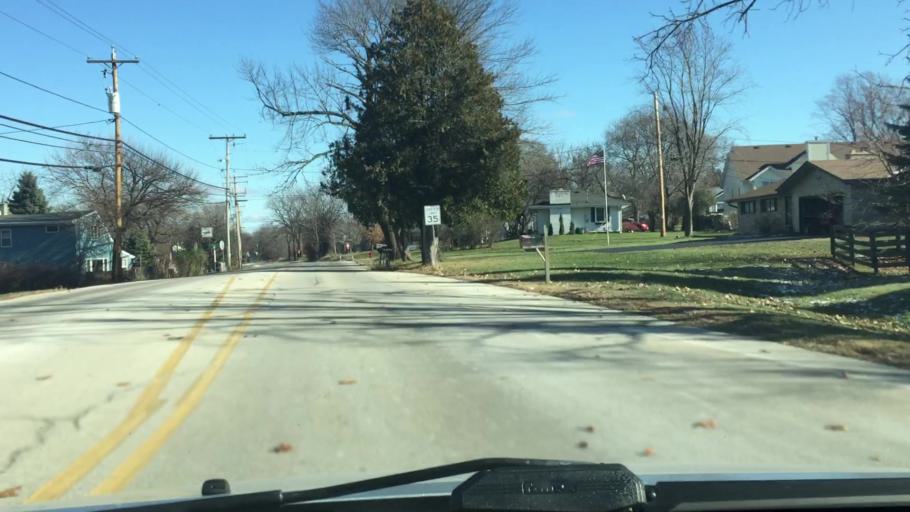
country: US
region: Wisconsin
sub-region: Waukesha County
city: Pewaukee
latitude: 43.0672
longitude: -88.2910
